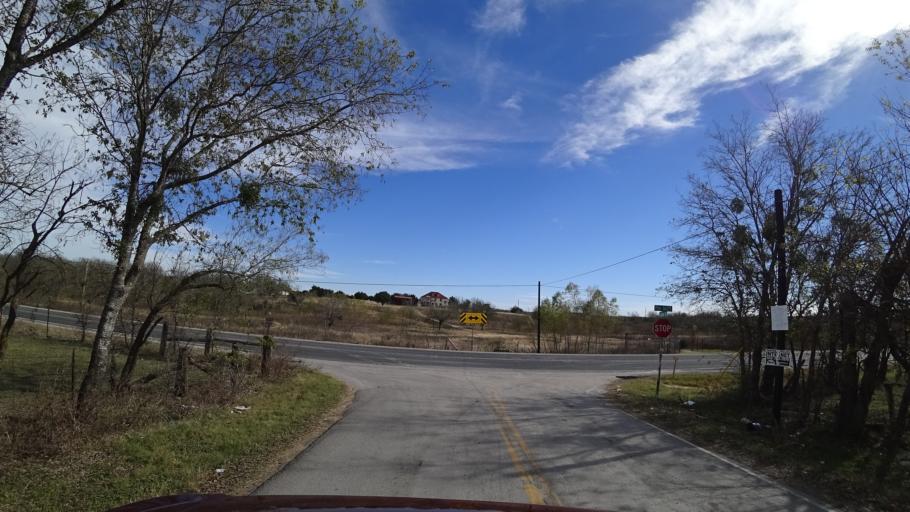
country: US
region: Texas
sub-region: Travis County
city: Onion Creek
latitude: 30.1140
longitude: -97.7197
